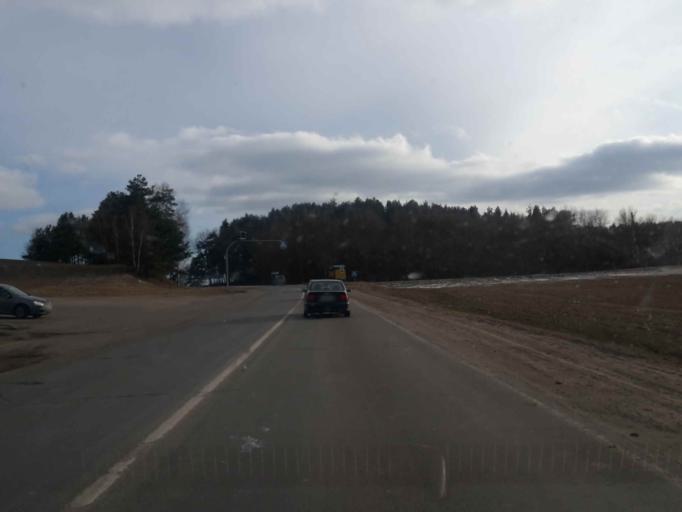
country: BY
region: Minsk
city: Bal'shavik
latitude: 54.0308
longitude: 27.5594
